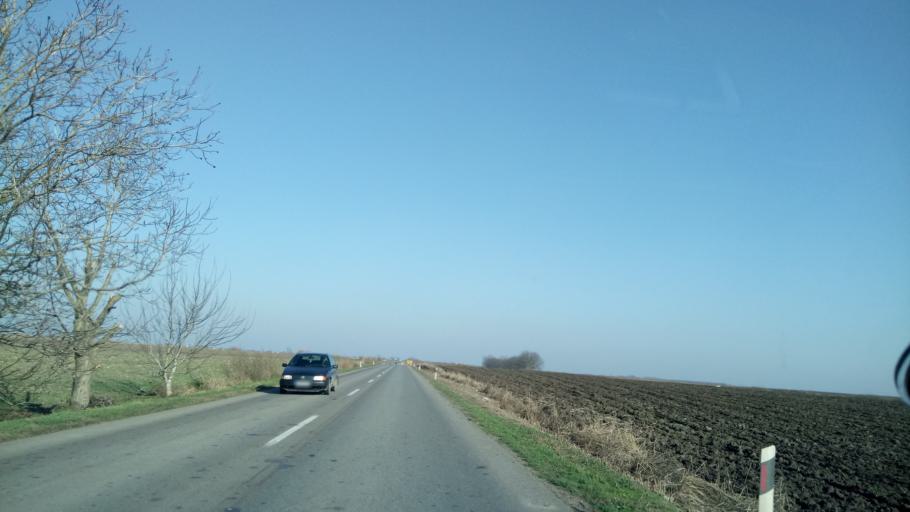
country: RS
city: Putinci
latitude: 45.0028
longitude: 20.0030
